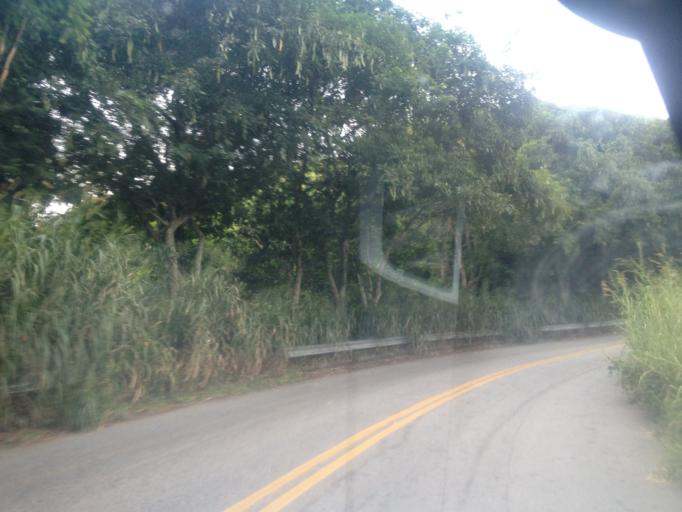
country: BR
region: Rio de Janeiro
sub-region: Quatis
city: Quatis
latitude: -22.3839
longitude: -44.2641
